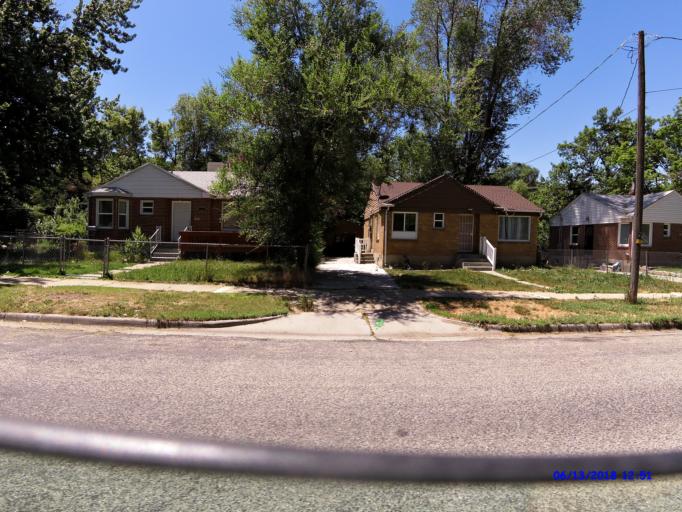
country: US
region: Utah
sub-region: Weber County
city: South Ogden
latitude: 41.2074
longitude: -111.9560
